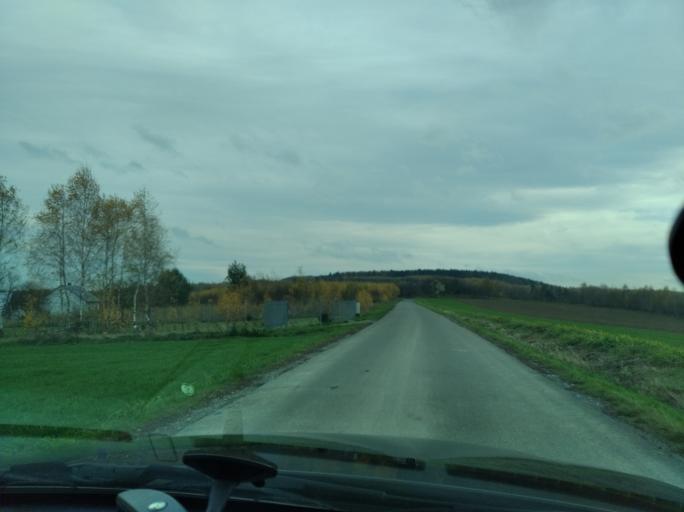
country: PL
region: Subcarpathian Voivodeship
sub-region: Powiat strzyzowski
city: Strzyzow
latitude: 49.9174
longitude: 21.7644
